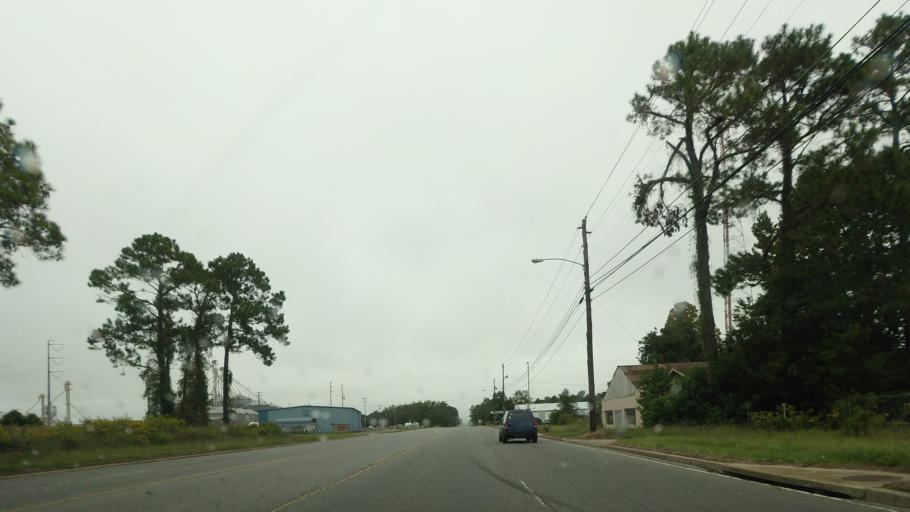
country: US
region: Georgia
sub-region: Irwin County
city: Ocilla
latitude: 31.6064
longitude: -83.2502
